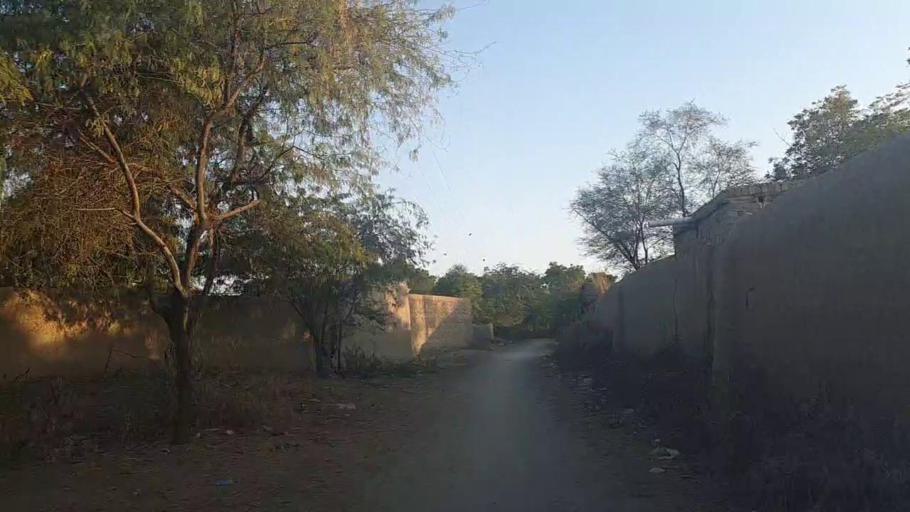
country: PK
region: Sindh
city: Jam Sahib
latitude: 26.3209
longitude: 68.7025
